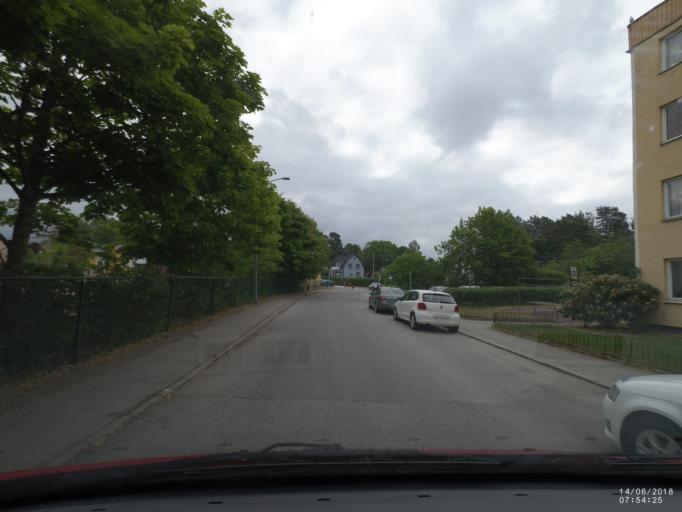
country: SE
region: Soedermanland
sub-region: Nykopings Kommun
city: Nykoping
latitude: 58.7603
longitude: 17.0241
